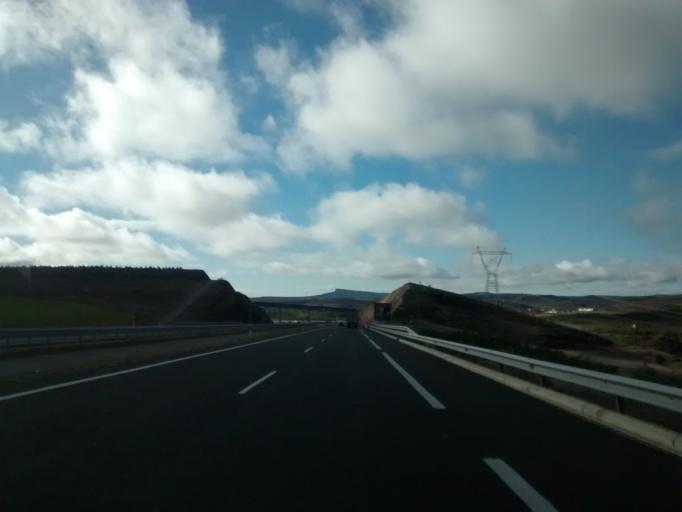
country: ES
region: Castille and Leon
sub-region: Provincia de Palencia
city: Aguilar de Campoo
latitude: 42.8028
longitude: -4.2326
